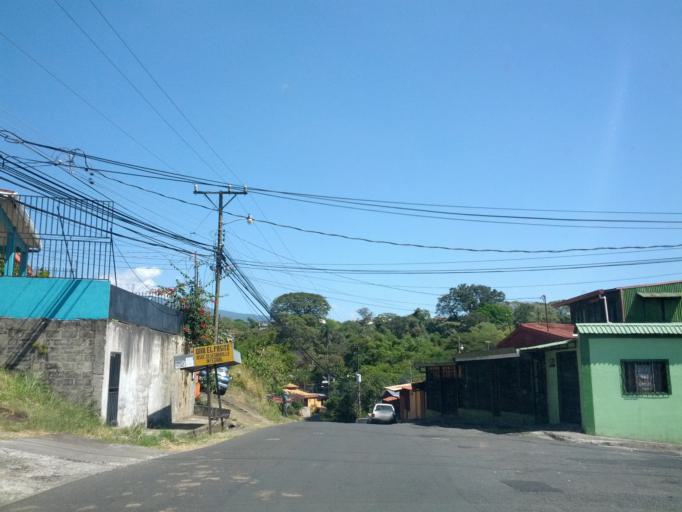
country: CR
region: Alajuela
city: Alajuela
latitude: 10.0079
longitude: -84.2016
